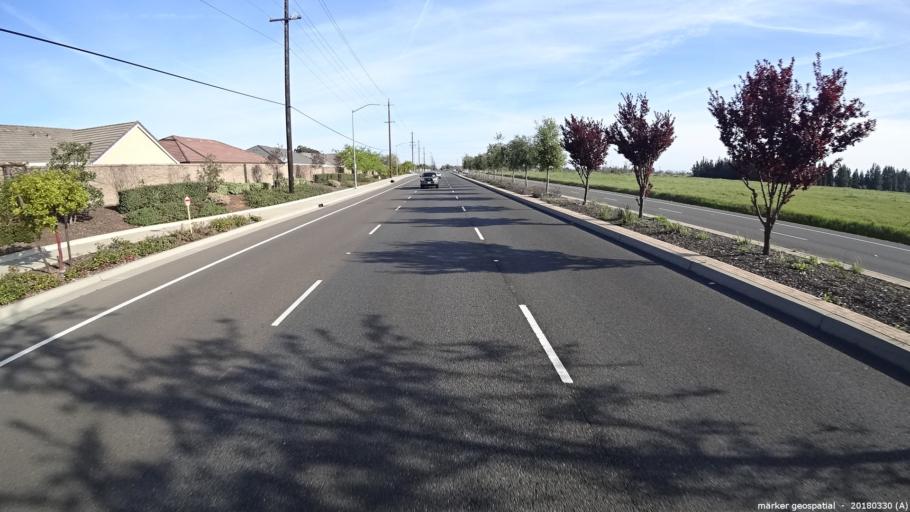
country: US
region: California
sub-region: Sacramento County
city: Vineyard
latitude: 38.4874
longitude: -121.3350
